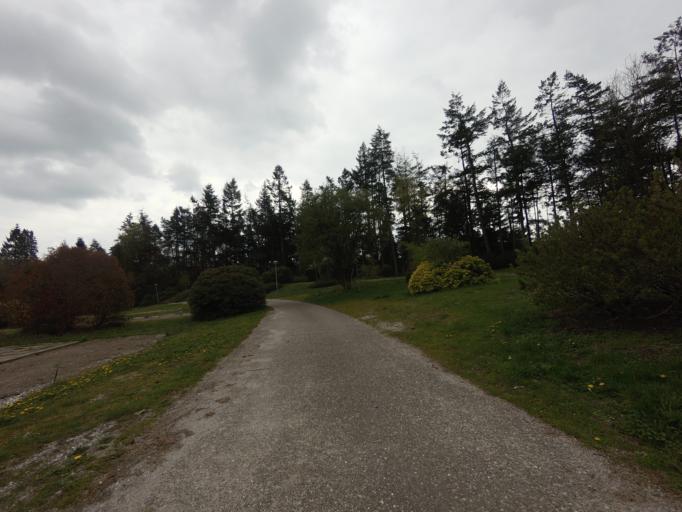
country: NL
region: Gelderland
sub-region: Gemeente Ede
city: Lunteren
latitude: 52.0964
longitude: 5.6451
